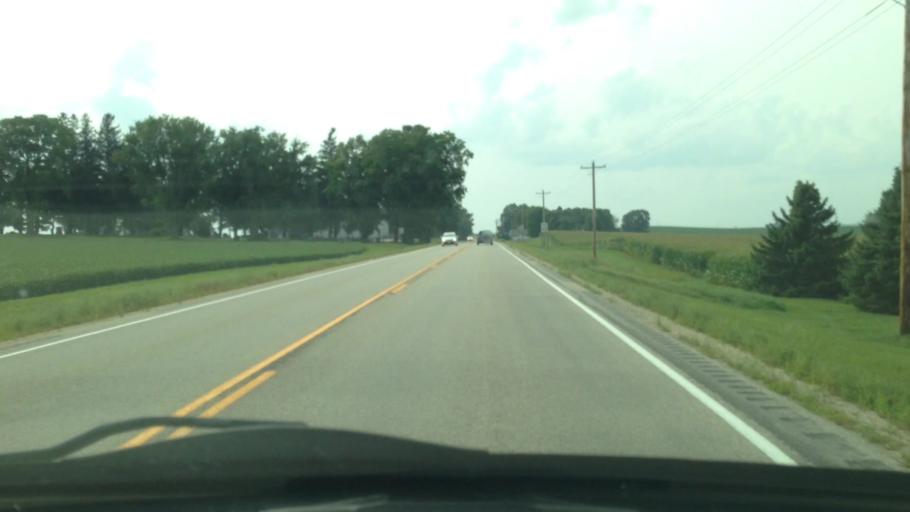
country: US
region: Minnesota
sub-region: Wabasha County
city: Elgin
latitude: 44.1657
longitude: -92.3321
